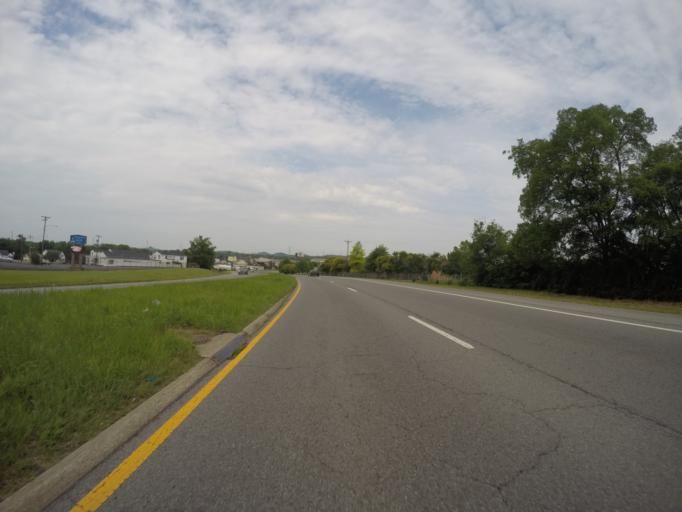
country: US
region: Tennessee
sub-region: Davidson County
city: Goodlettsville
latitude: 36.2640
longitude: -86.7082
